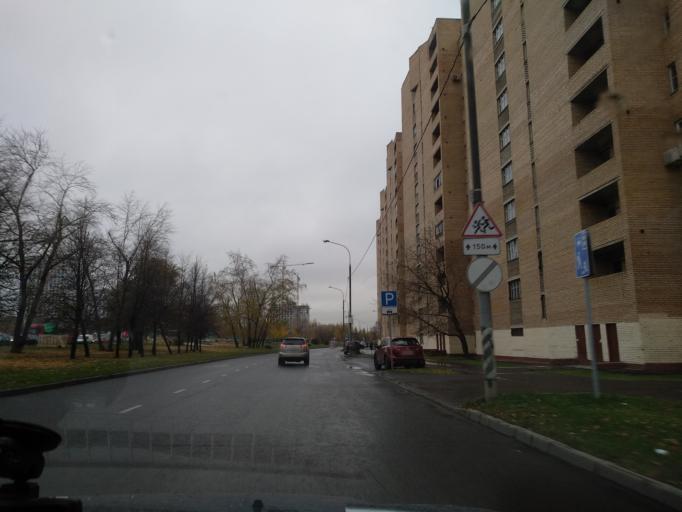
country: RU
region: Moscow
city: Otradnoye
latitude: 55.8712
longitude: 37.5942
